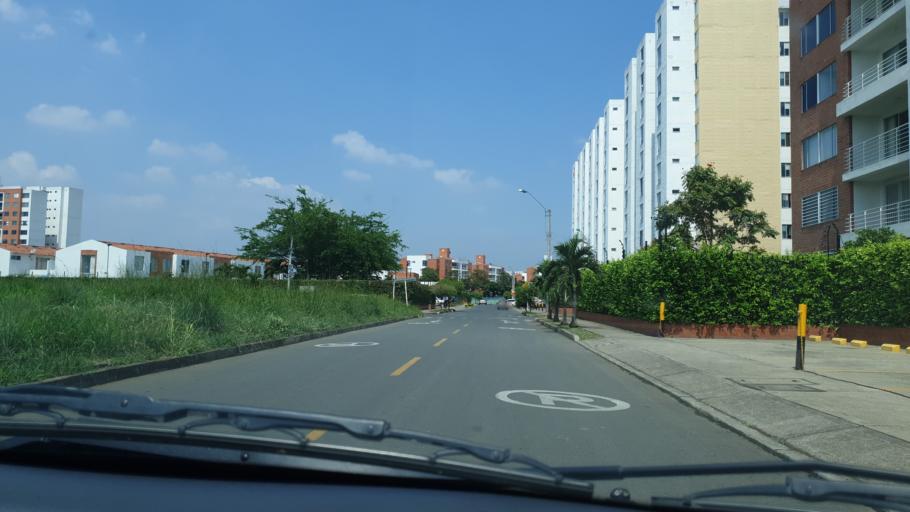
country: CO
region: Valle del Cauca
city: Cali
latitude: 3.3659
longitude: -76.5221
